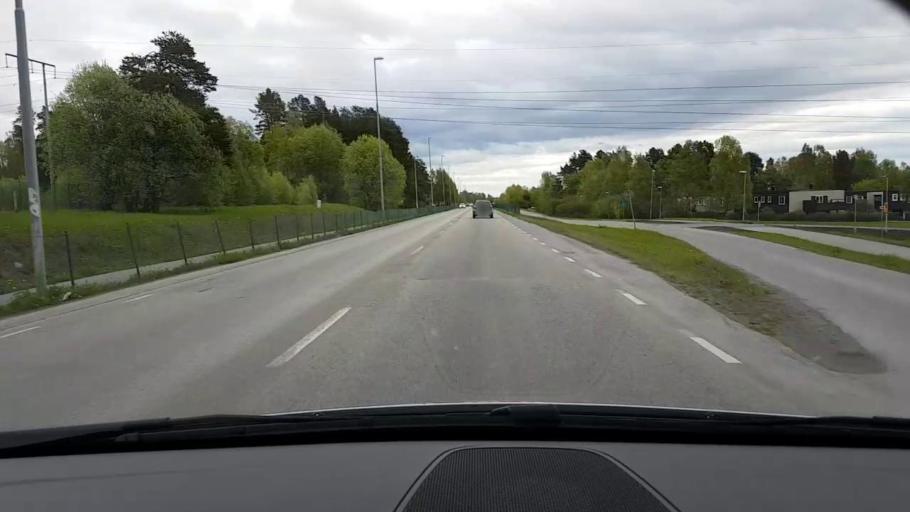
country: SE
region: Jaemtland
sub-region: OEstersunds Kommun
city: Ostersund
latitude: 63.1584
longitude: 14.6728
